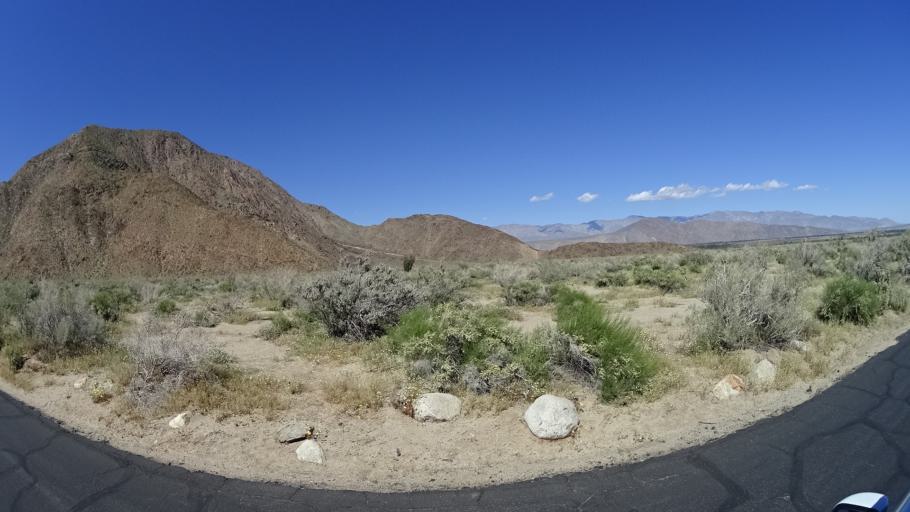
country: US
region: California
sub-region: San Diego County
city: Borrego Springs
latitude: 33.2703
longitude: -116.4132
